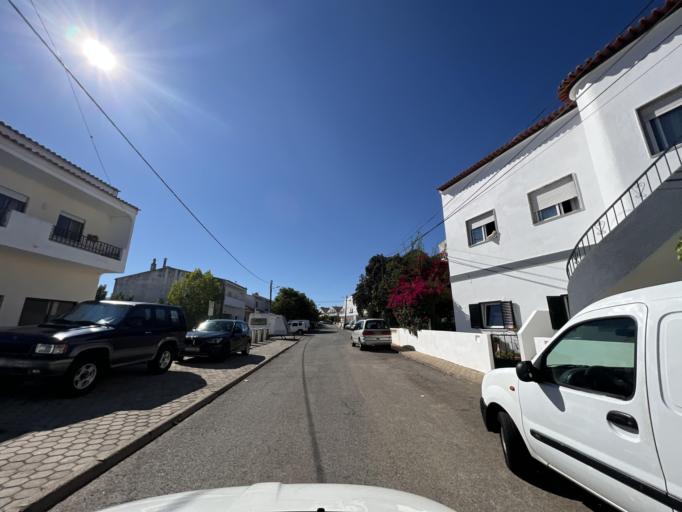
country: PT
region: Faro
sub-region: Lagoa
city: Estombar
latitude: 37.1441
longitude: -8.5101
